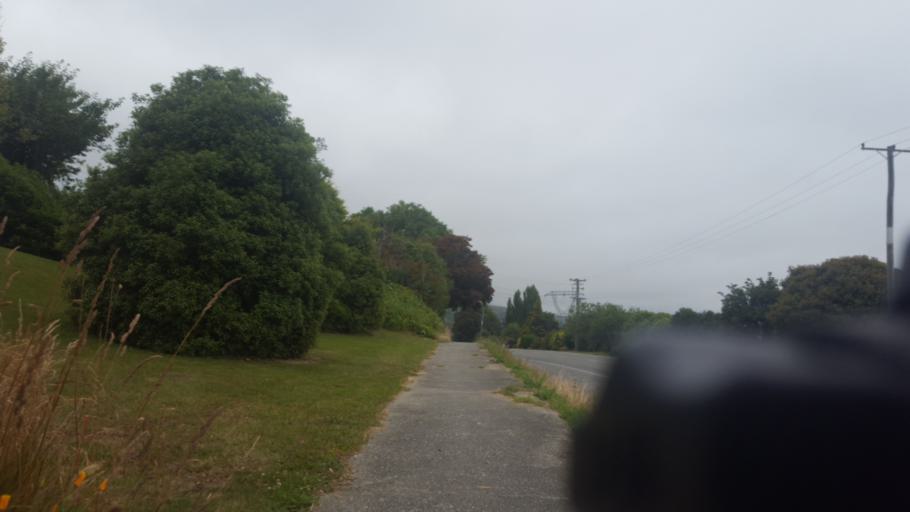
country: NZ
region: Otago
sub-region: Queenstown-Lakes District
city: Kingston
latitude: -45.5311
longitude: 169.2989
